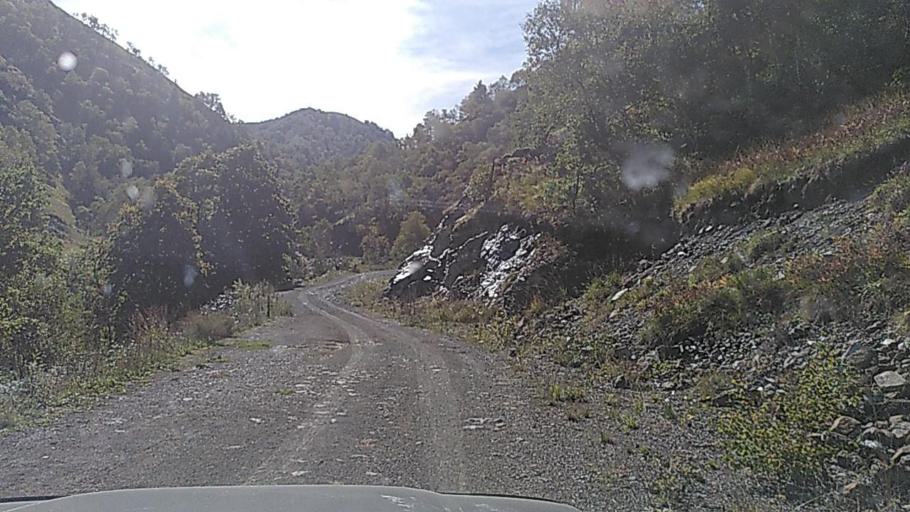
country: RU
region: Kabardino-Balkariya
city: Kamennomostskoye
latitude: 43.7166
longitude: 42.8452
